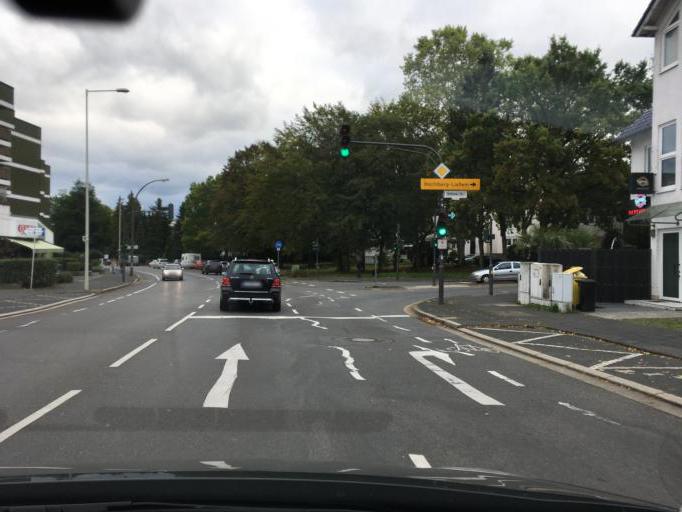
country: DE
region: North Rhine-Westphalia
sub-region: Regierungsbezirk Koln
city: Konigswinter
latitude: 50.6642
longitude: 7.1761
